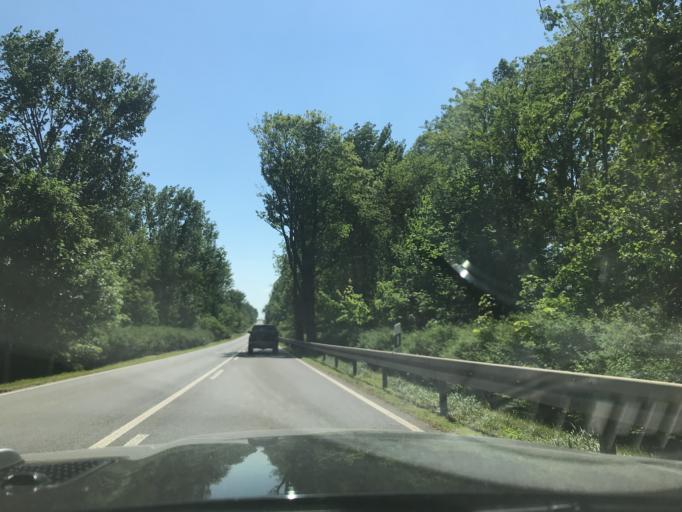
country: DE
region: Thuringia
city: Hochheim
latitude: 51.0309
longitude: 10.6726
